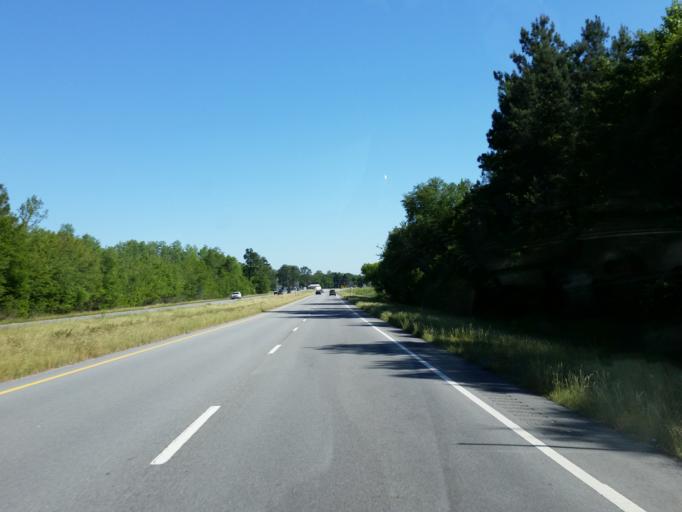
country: US
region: Georgia
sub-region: Lowndes County
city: Valdosta
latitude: 30.7064
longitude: -83.2124
